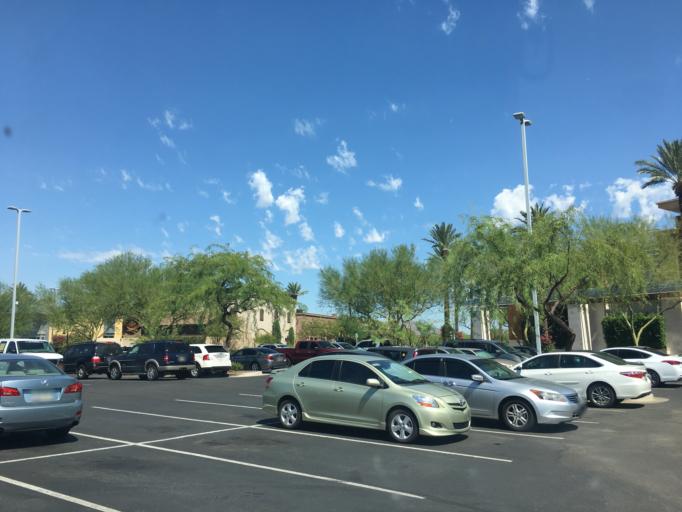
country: US
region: Arizona
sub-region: Maricopa County
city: Tempe
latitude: 33.4318
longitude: -111.9055
